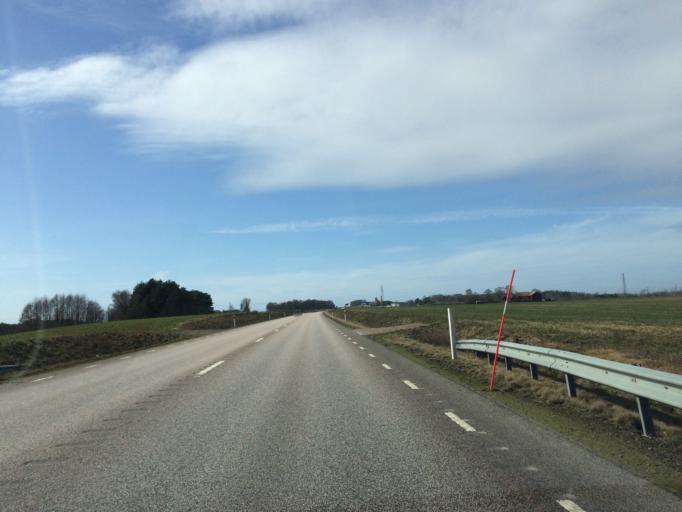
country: SE
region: Halland
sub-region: Laholms Kommun
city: Veinge
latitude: 56.5428
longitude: 13.1105
